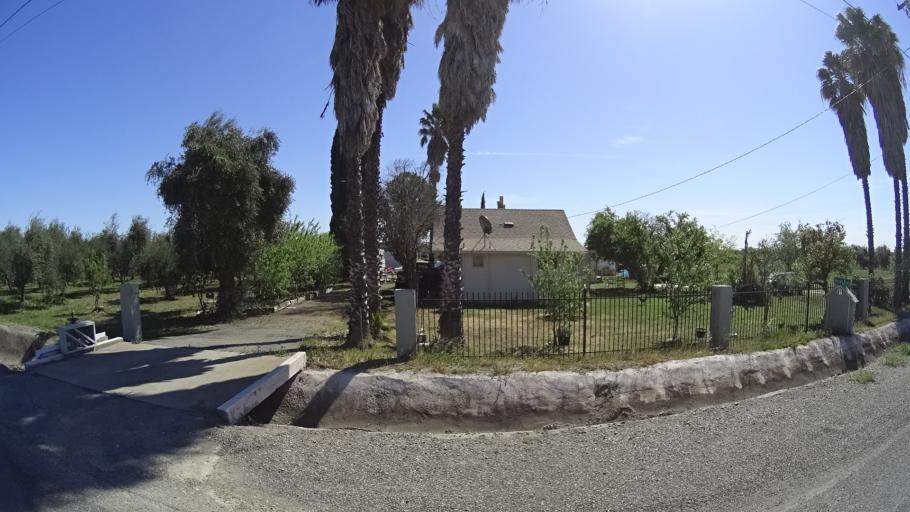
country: US
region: California
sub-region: Glenn County
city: Hamilton City
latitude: 39.7201
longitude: -122.1043
